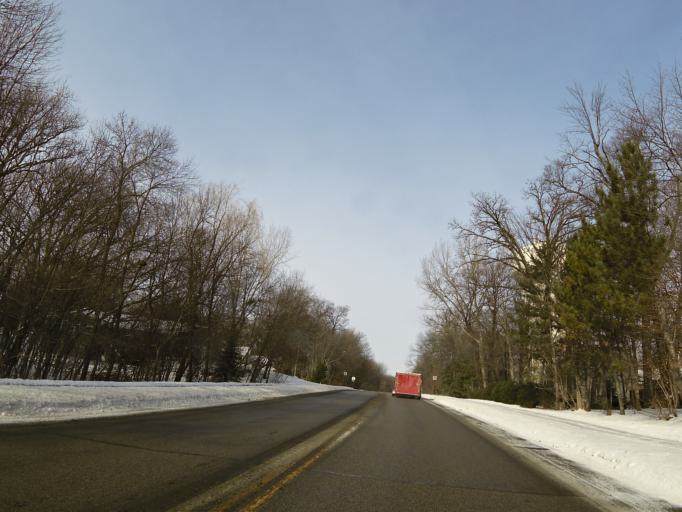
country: US
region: Minnesota
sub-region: Carver County
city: Chanhassen
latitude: 44.8682
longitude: -93.5117
